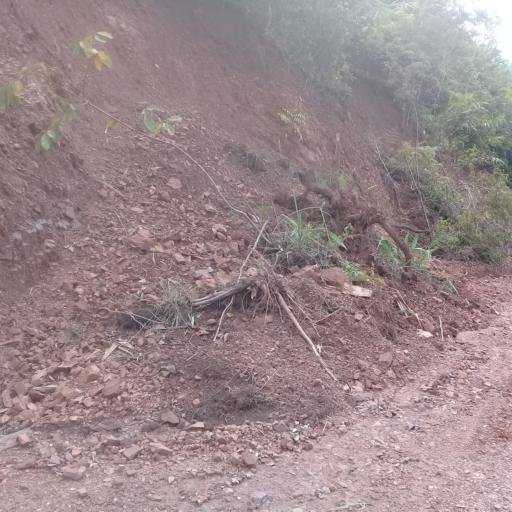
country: VN
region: Huyen Dien Bien
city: Thi Tran Muong Cha
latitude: 21.6775
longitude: 102.9138
